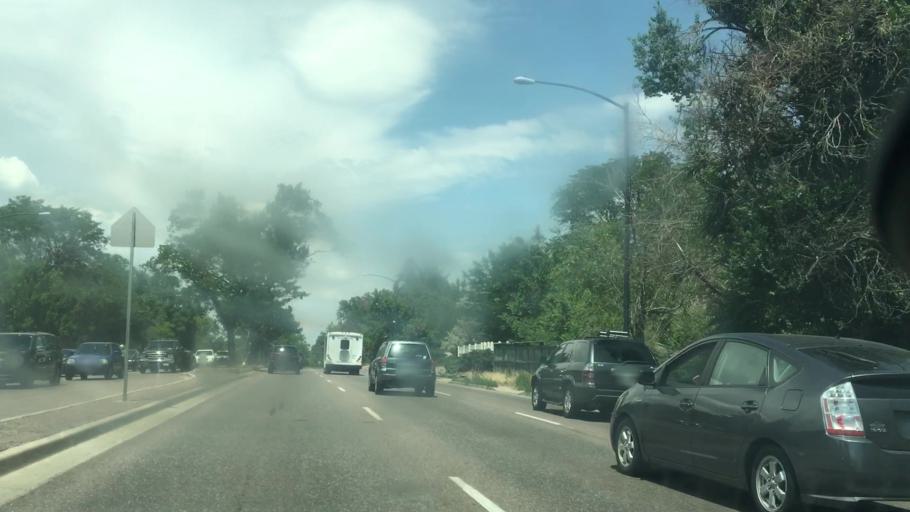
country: US
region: Colorado
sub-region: Arapahoe County
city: Glendale
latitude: 39.7215
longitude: -104.9407
